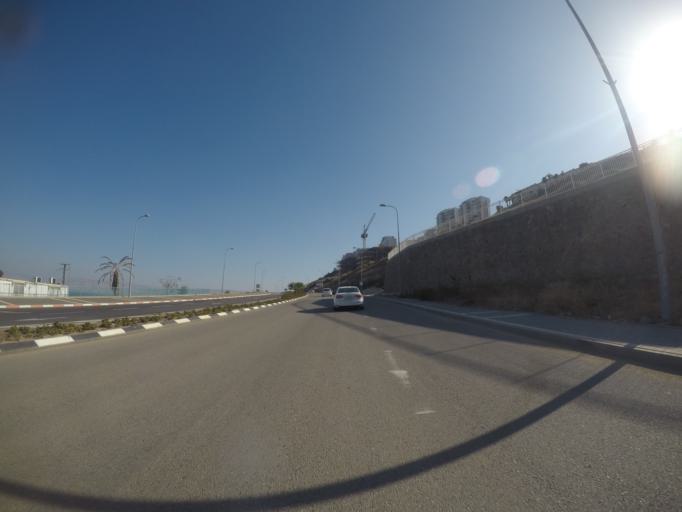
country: IL
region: Northern District
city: Tiberias
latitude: 32.8004
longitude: 35.5325
